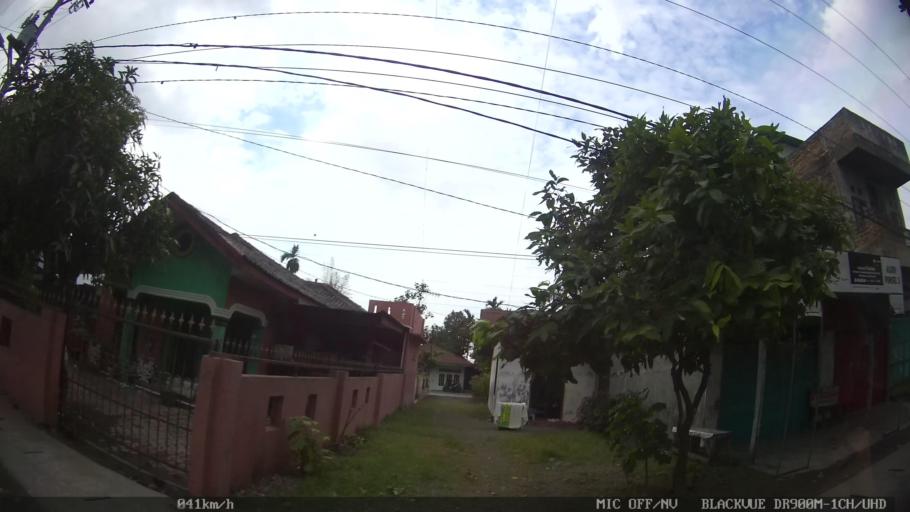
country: ID
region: North Sumatra
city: Sunggal
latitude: 3.6184
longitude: 98.6147
